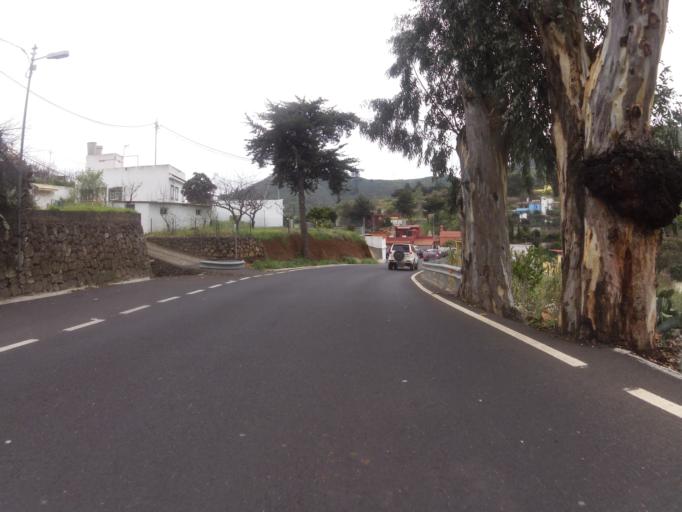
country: ES
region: Canary Islands
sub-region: Provincia de Las Palmas
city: Vega de San Mateo
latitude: 28.0072
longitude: -15.5421
